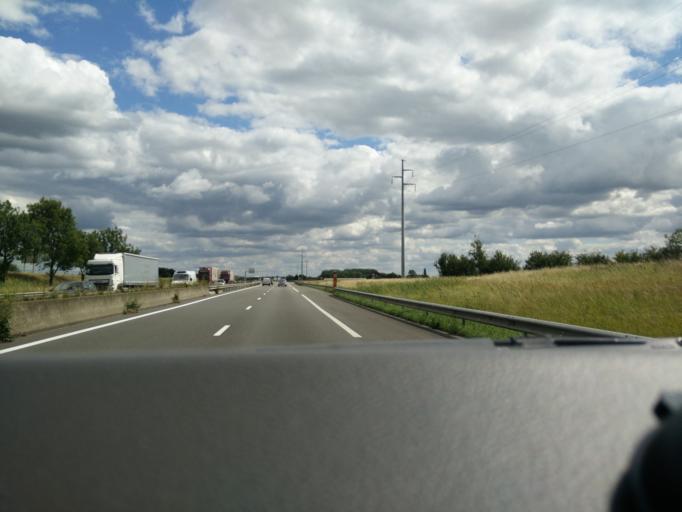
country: FR
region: Nord-Pas-de-Calais
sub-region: Departement du Nord
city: Herzeele
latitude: 50.8854
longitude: 2.5150
